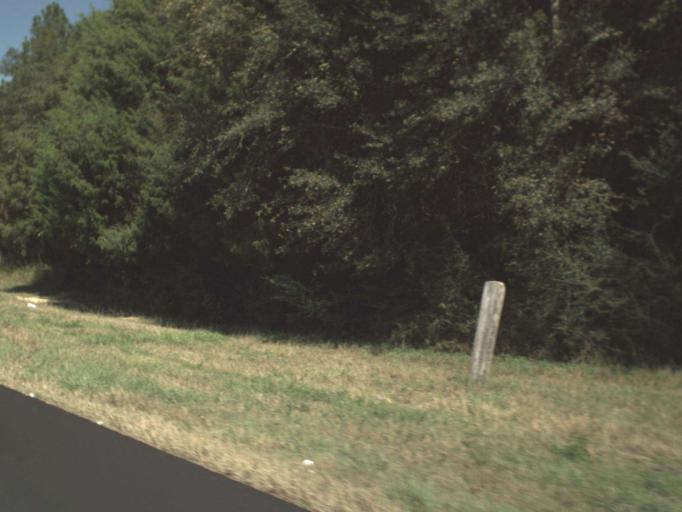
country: US
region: Florida
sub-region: Walton County
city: DeFuniak Springs
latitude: 30.8310
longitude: -86.2317
